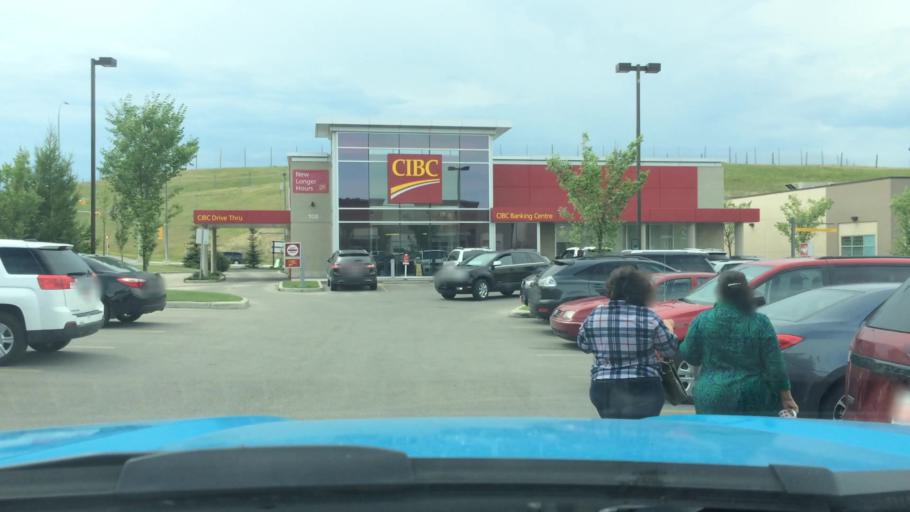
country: CA
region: Alberta
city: Calgary
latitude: 51.1604
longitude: -114.1611
